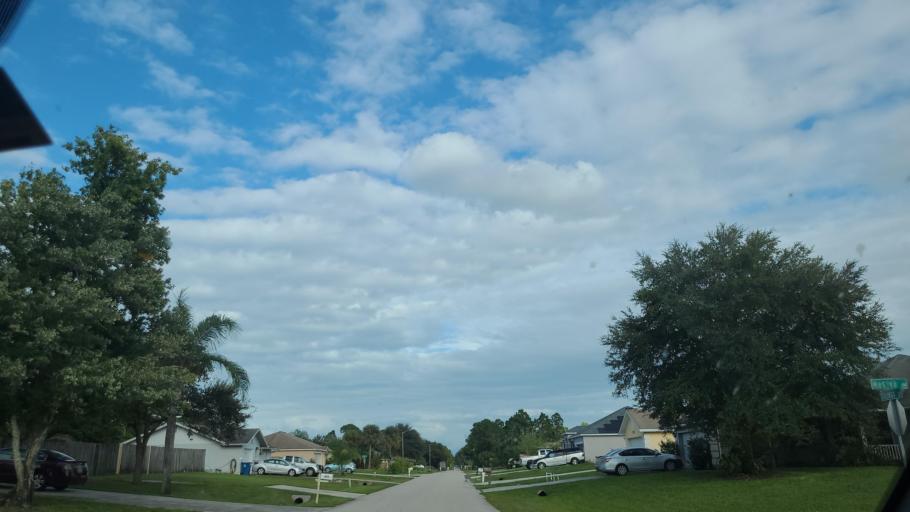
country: US
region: Florida
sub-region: Brevard County
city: West Melbourne
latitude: 27.9765
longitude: -80.6685
